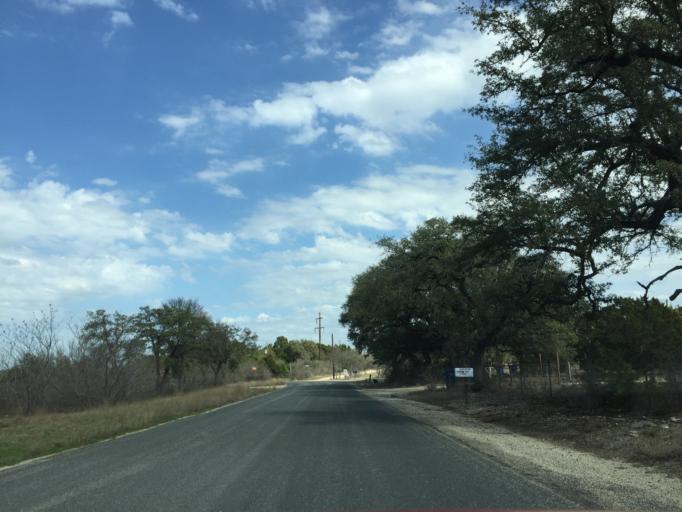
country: US
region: Texas
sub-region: Burnet County
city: Bertram
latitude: 30.7512
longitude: -97.9382
